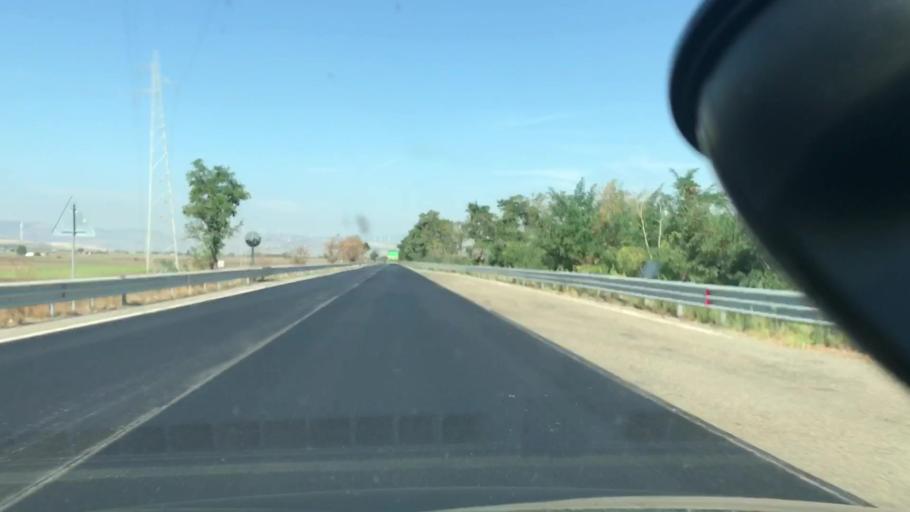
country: IT
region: Basilicate
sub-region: Provincia di Potenza
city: Zona 179
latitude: 41.0769
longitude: 15.6389
